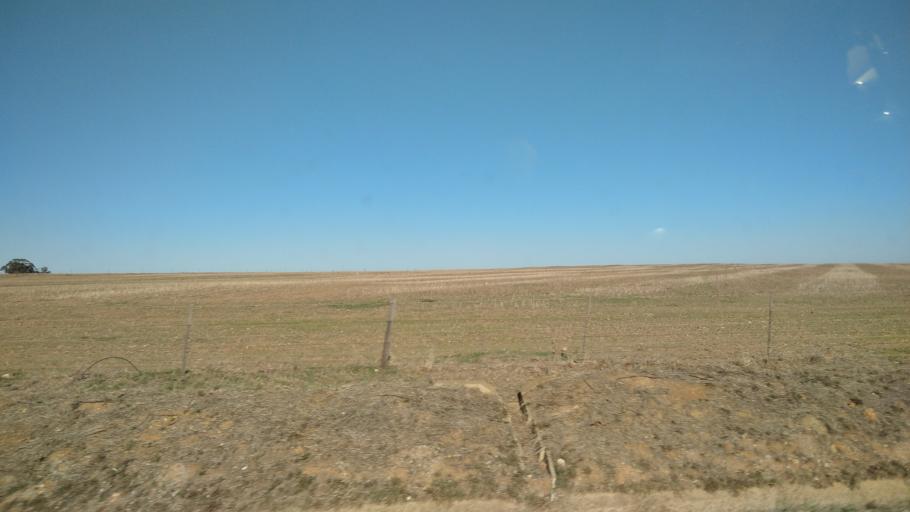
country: ZA
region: Western Cape
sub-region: West Coast District Municipality
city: Malmesbury
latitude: -33.3535
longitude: 18.6429
